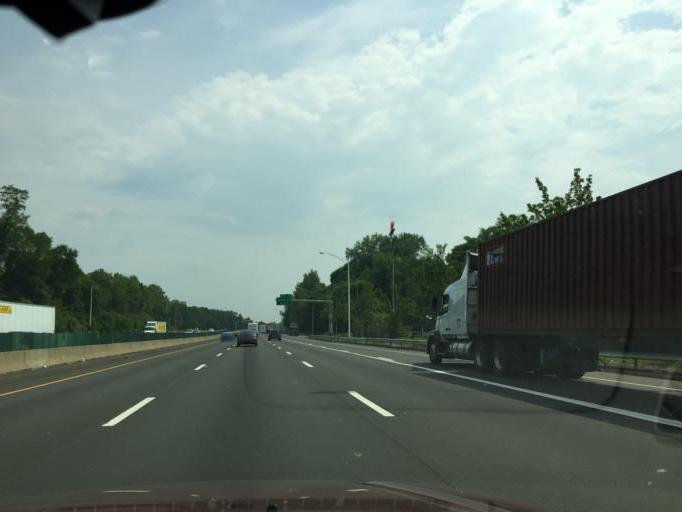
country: US
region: Connecticut
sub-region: Fairfield County
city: Greenwich
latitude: 41.0149
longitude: -73.6385
